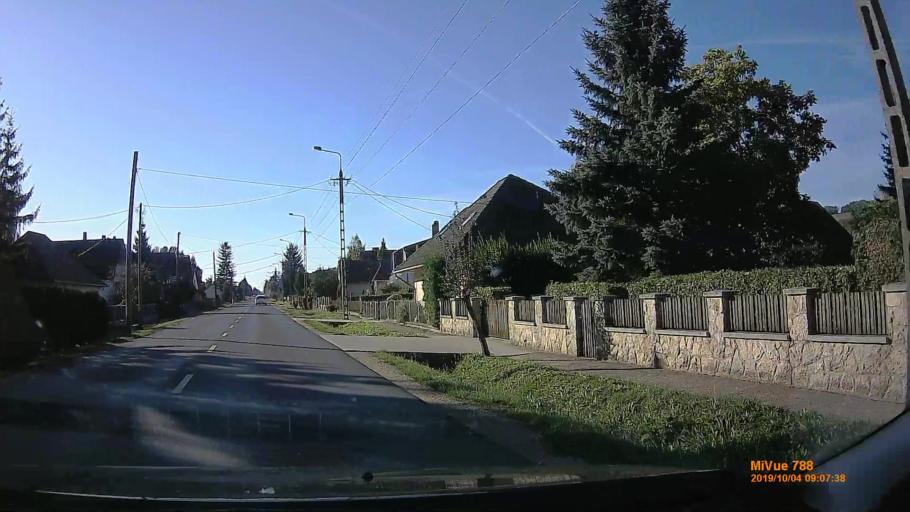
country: HU
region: Somogy
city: Karad
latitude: 46.6772
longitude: 17.7747
